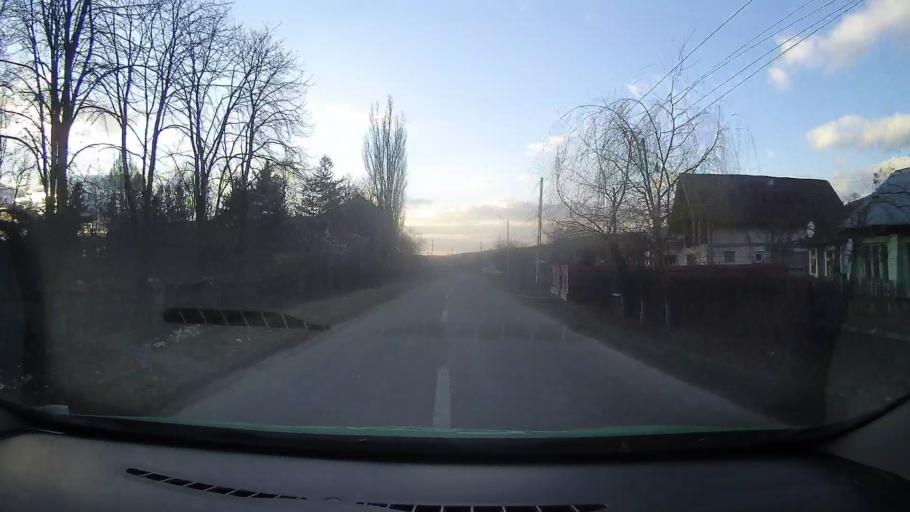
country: RO
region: Dambovita
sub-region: Comuna Gura Ocnitei
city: Gura Ocnitei
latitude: 44.9377
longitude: 25.5833
